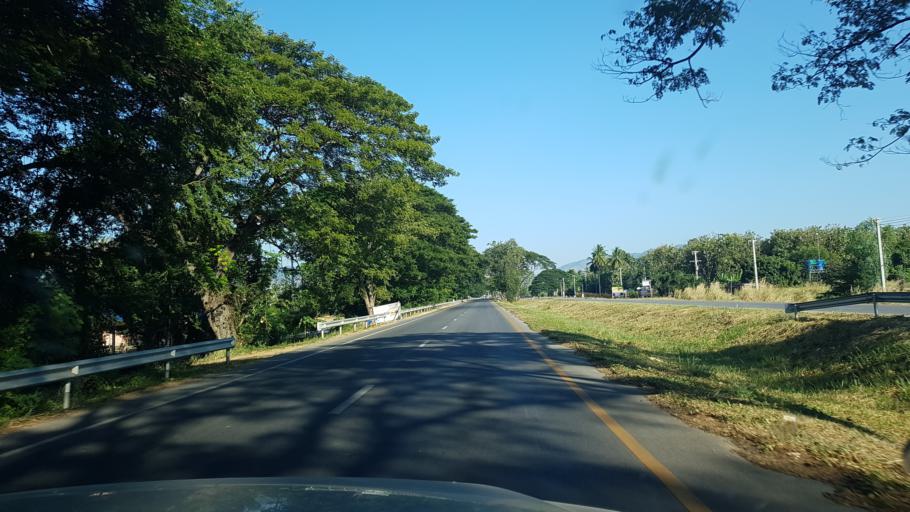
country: TH
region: Phetchabun
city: Lom Sak
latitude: 16.7268
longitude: 101.2505
